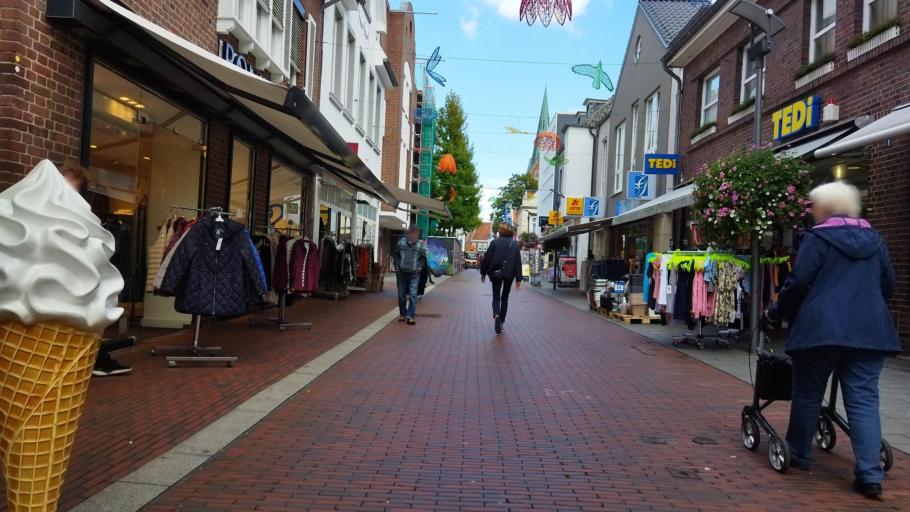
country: DE
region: Lower Saxony
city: Lingen
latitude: 52.5212
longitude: 7.3169
